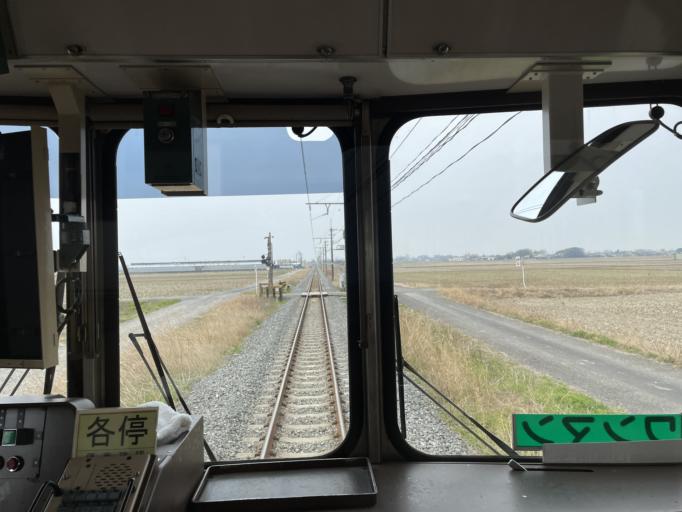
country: JP
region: Saitama
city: Hanyu
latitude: 36.1692
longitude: 139.5052
